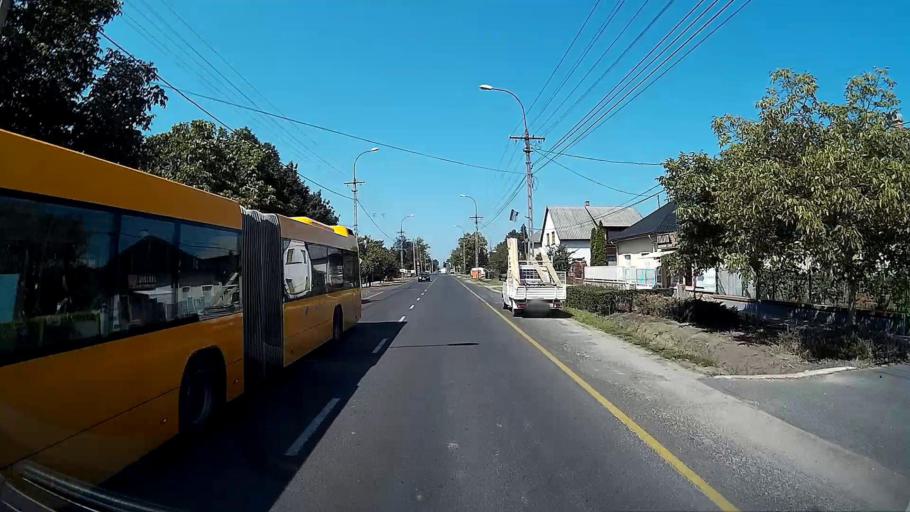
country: HU
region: Pest
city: Vecses
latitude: 47.4130
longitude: 19.2667
